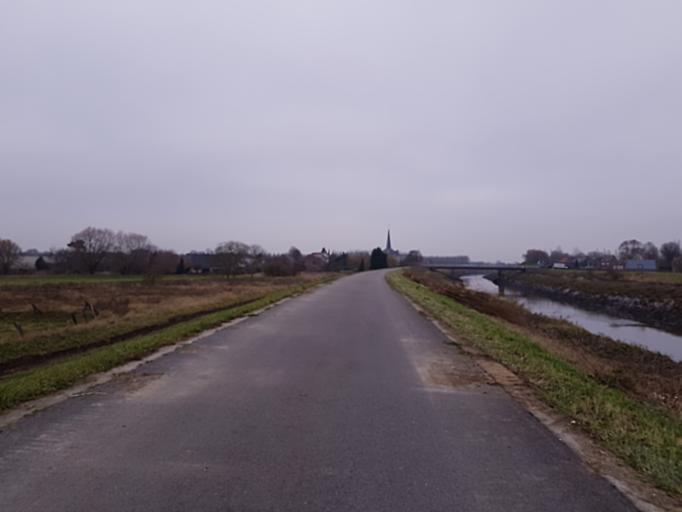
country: BE
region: Flanders
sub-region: Provincie Antwerpen
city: Rumst
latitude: 51.0433
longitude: 4.4195
